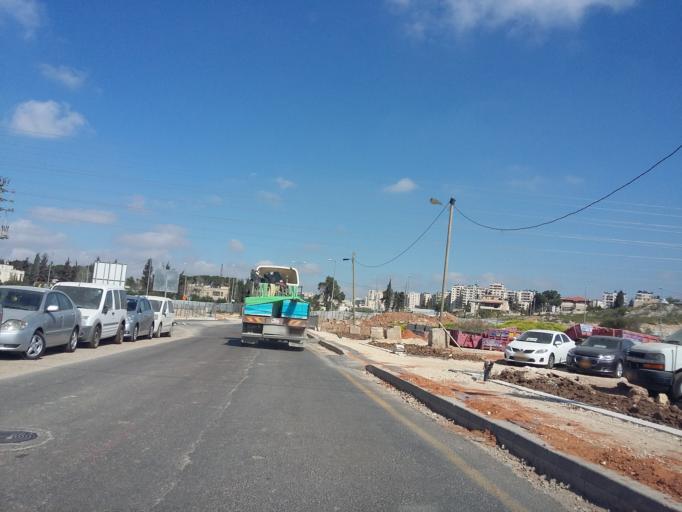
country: PS
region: West Bank
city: Qalandiya
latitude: 31.8595
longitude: 35.2216
